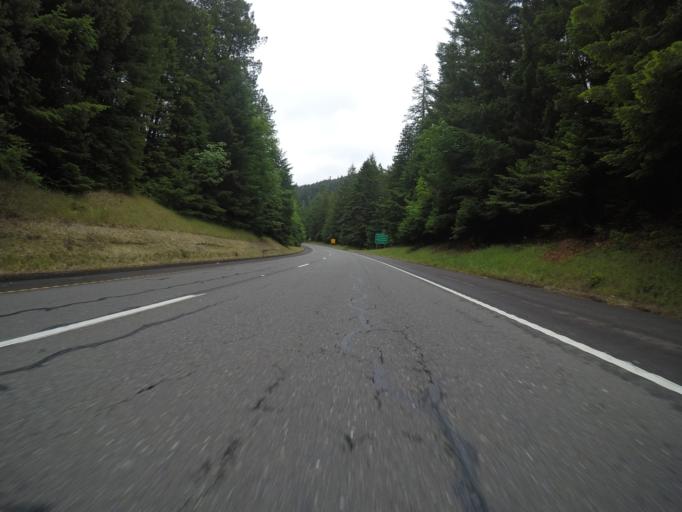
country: US
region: California
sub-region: Humboldt County
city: Rio Dell
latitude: 40.4425
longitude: -124.0393
